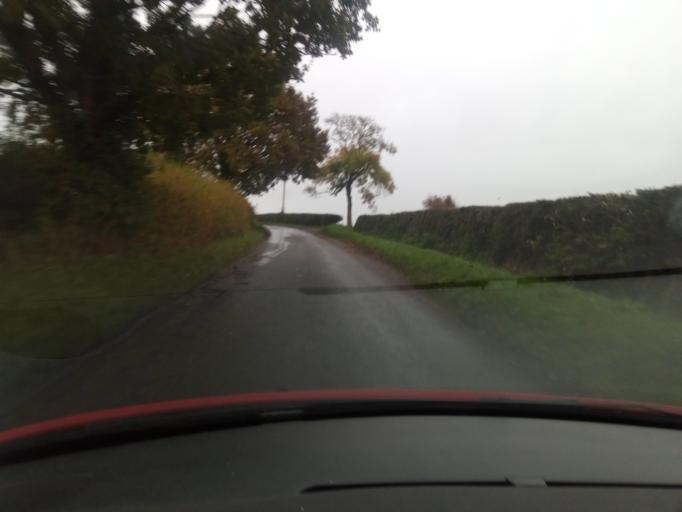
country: GB
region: England
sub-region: Derbyshire
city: Borrowash
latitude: 52.8649
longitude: -1.4006
